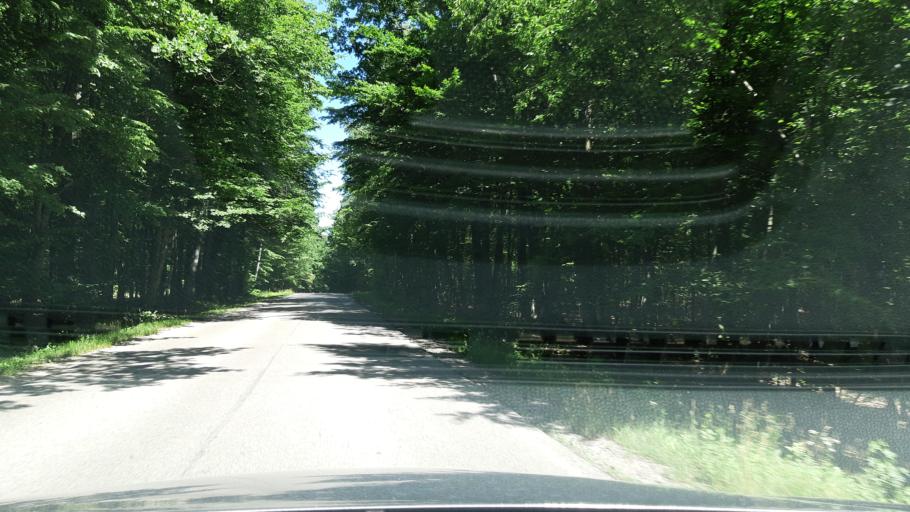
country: PL
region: Warmian-Masurian Voivodeship
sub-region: Powiat piski
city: Ruciane-Nida
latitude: 53.7289
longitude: 21.5028
